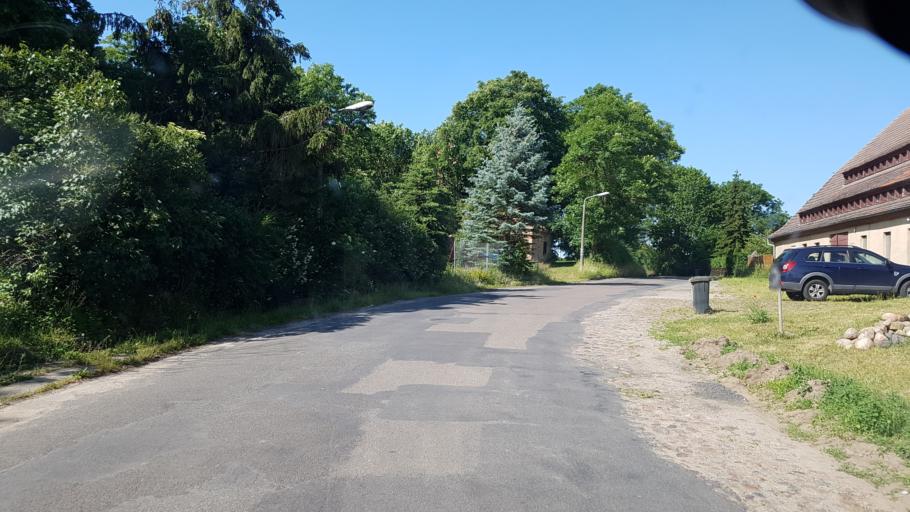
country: DE
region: Brandenburg
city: Gramzow
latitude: 53.2588
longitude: 13.9756
